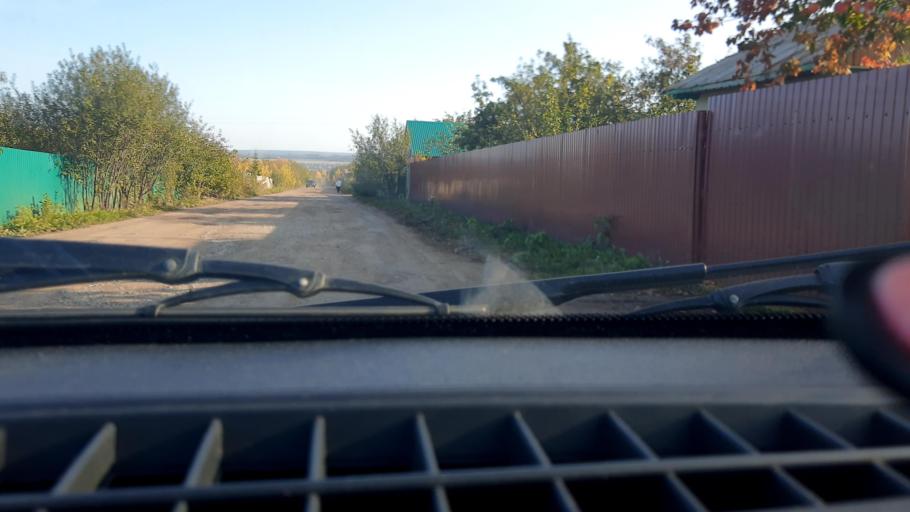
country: RU
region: Bashkortostan
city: Avdon
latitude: 54.5751
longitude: 55.7332
